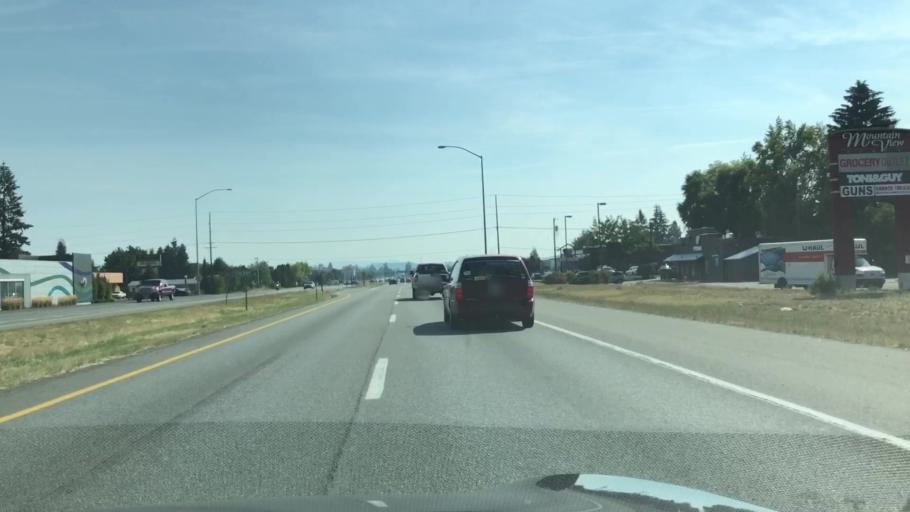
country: US
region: Idaho
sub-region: Kootenai County
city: Coeur d'Alene
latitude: 47.7062
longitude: -116.7917
